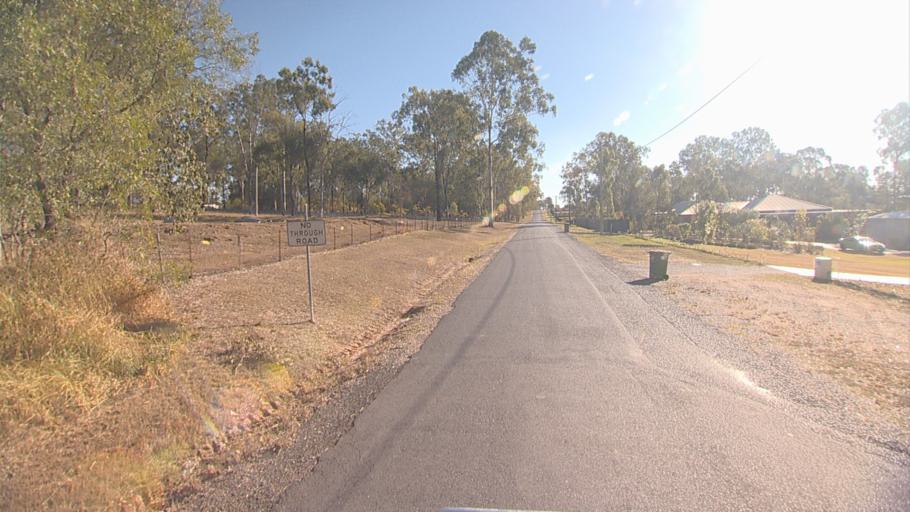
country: AU
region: Queensland
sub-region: Logan
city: North Maclean
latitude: -27.7963
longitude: 153.0260
